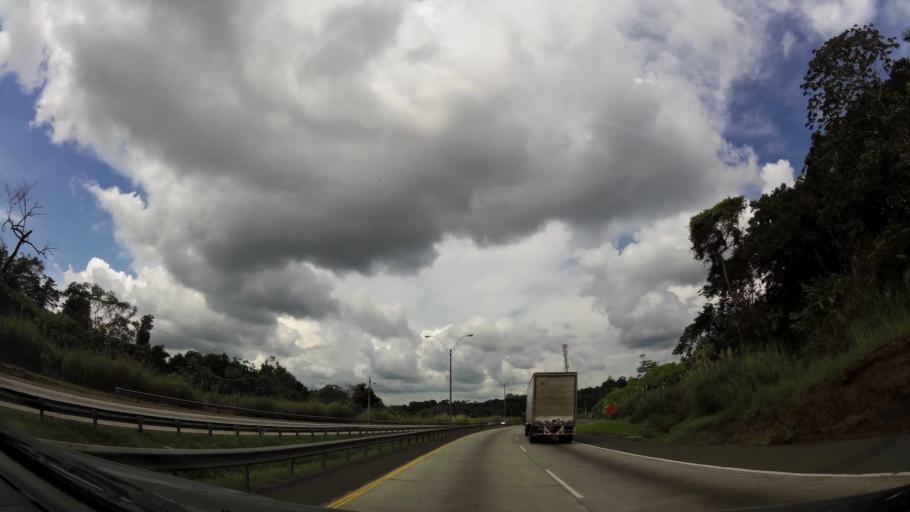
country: PA
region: Panama
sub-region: Distrito de Panama
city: Paraiso
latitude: 8.9953
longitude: -79.6518
